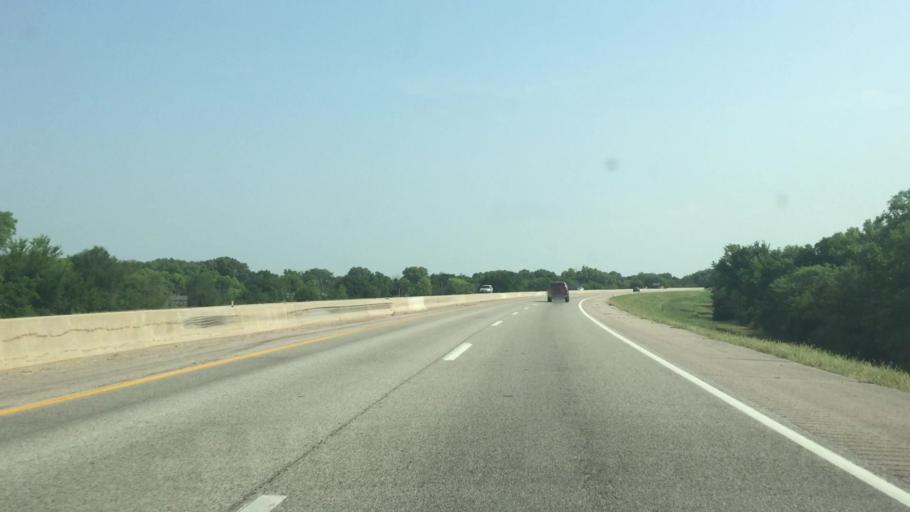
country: US
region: Kansas
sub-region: Butler County
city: El Dorado
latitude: 37.8651
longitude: -96.8581
